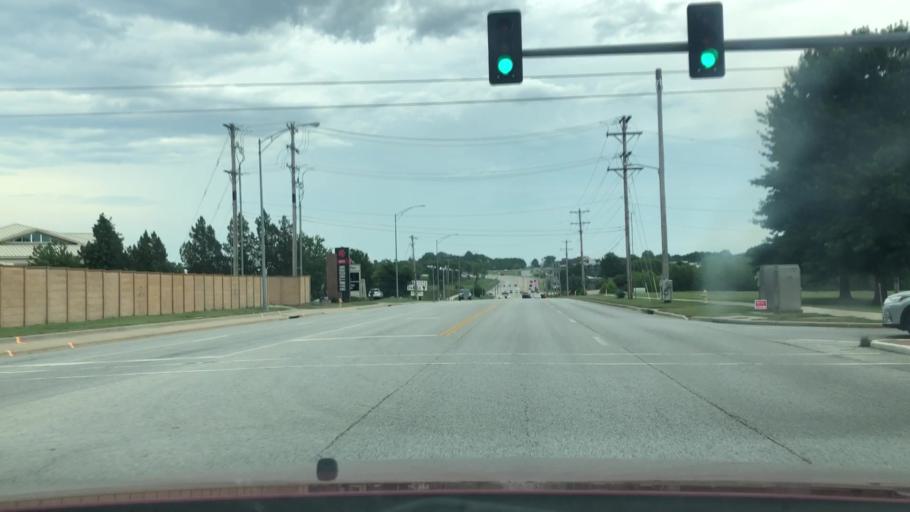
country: US
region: Missouri
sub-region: Greene County
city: Springfield
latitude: 37.1373
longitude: -93.2630
